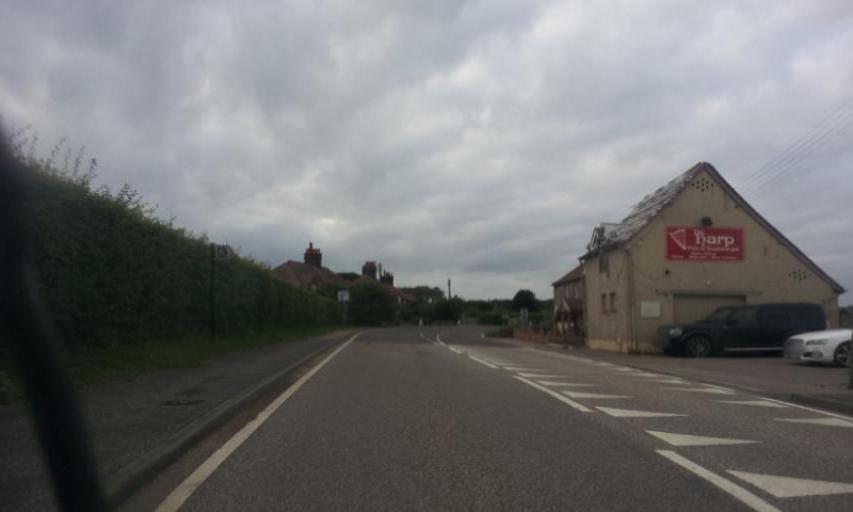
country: GB
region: England
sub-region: Kent
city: East Peckham
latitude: 51.2207
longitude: 0.3944
